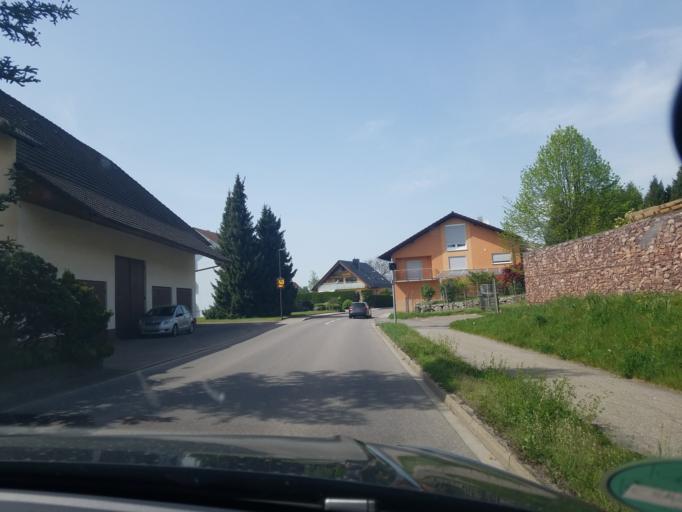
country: DE
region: Baden-Wuerttemberg
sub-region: Freiburg Region
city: Haslach
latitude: 48.5639
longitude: 8.0581
